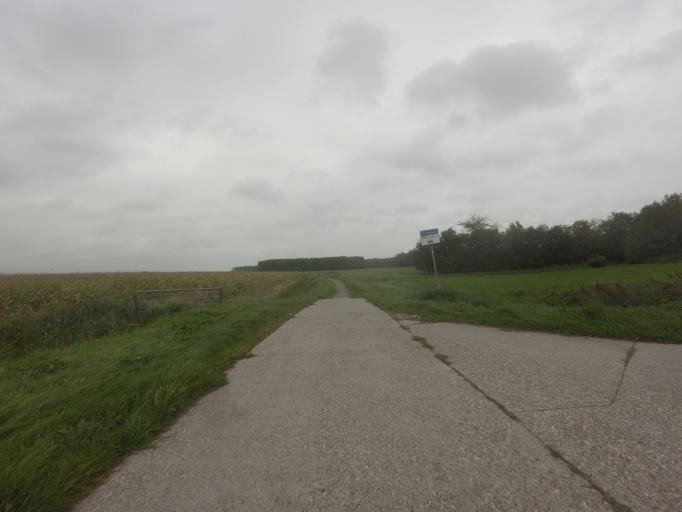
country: NL
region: Friesland
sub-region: Gemeente Leeuwarden
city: Bilgaard
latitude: 53.2265
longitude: 5.7916
